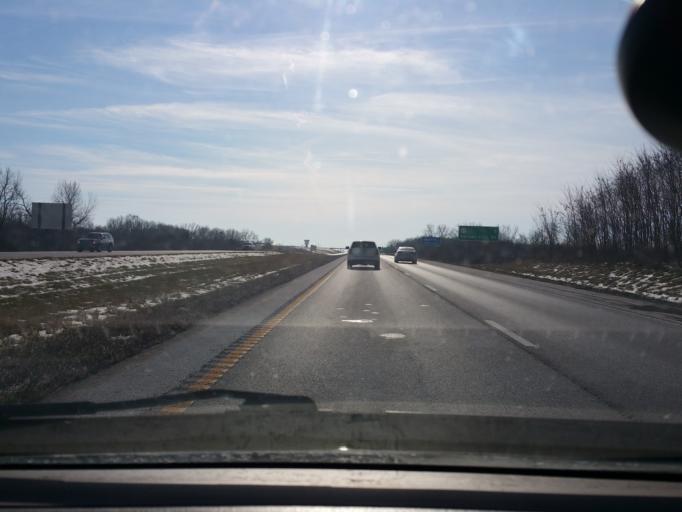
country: US
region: Missouri
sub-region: Clinton County
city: Cameron
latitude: 39.7415
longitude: -94.2204
